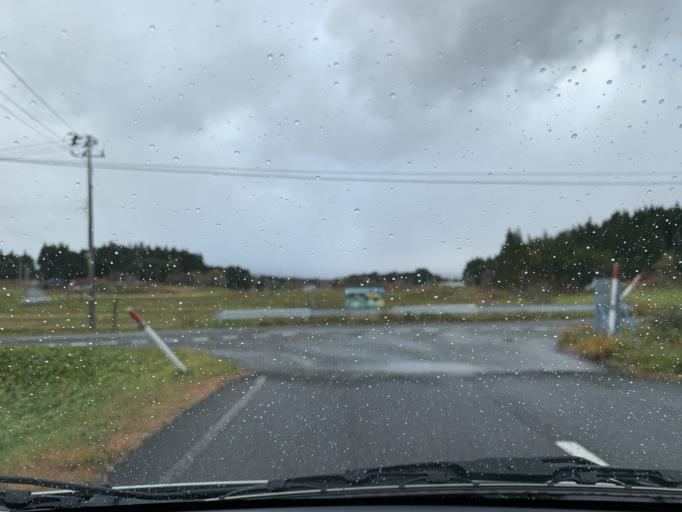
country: JP
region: Iwate
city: Mizusawa
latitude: 39.0891
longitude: 141.0003
